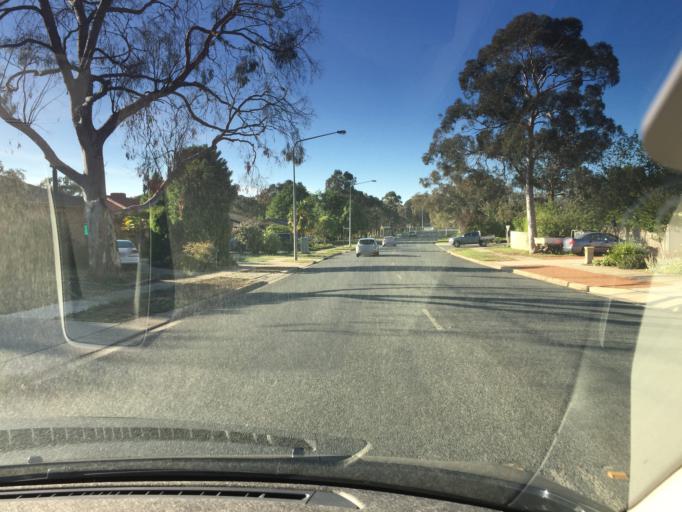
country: AU
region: Australian Capital Territory
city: Kaleen
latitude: -35.2199
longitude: 149.1112
